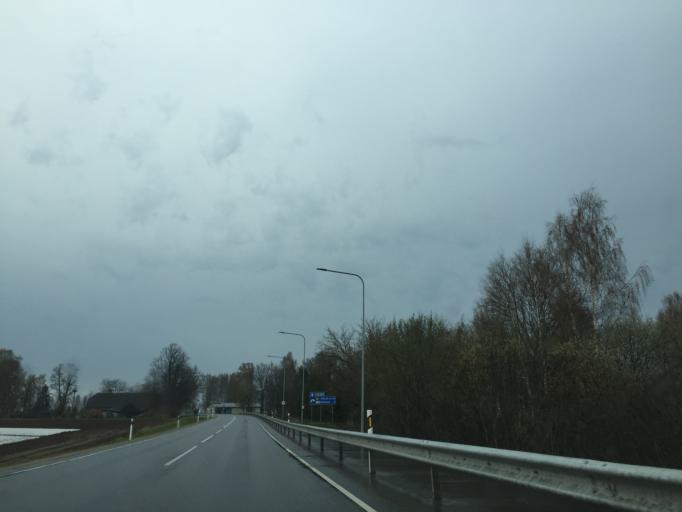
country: EE
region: Tartu
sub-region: UElenurme vald
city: Ulenurme
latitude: 58.2331
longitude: 26.6944
